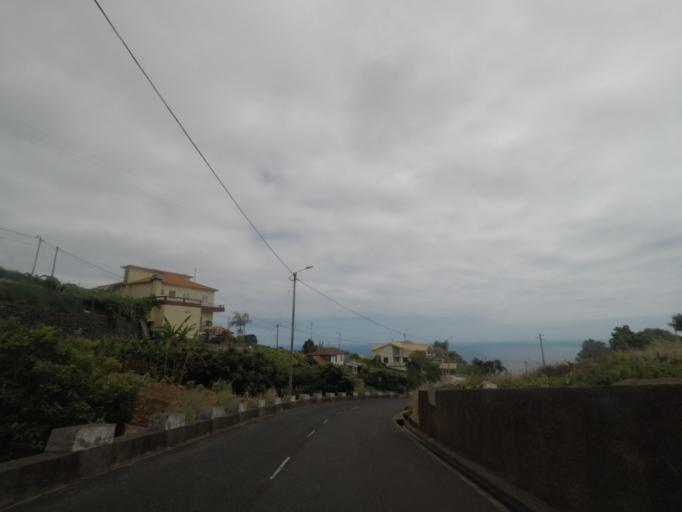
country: PT
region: Madeira
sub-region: Calheta
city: Estreito da Calheta
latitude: 32.7374
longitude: -17.1715
